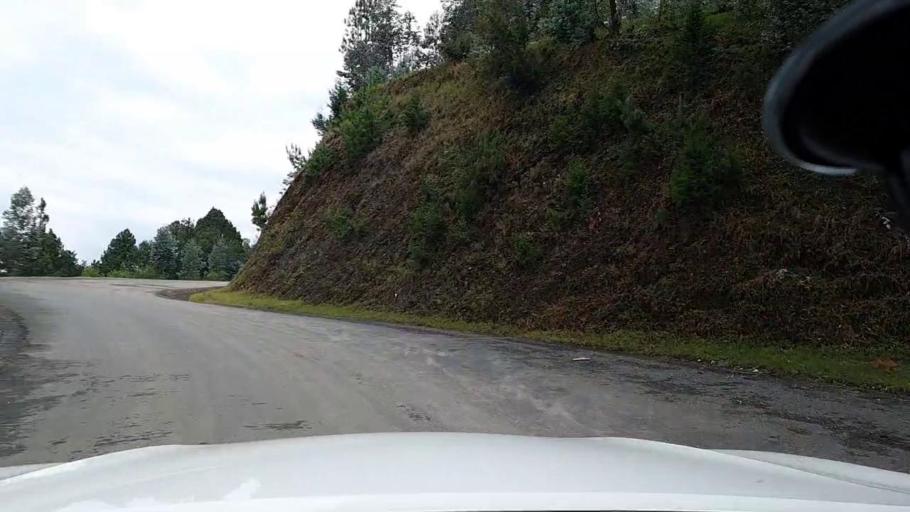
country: RW
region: Southern Province
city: Gitarama
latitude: -2.0647
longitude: 29.5596
